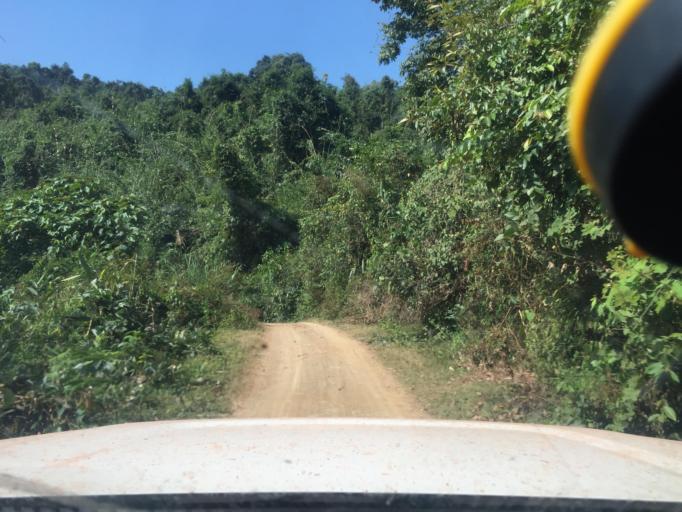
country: LA
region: Phongsali
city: Phongsali
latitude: 21.6589
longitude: 102.4184
